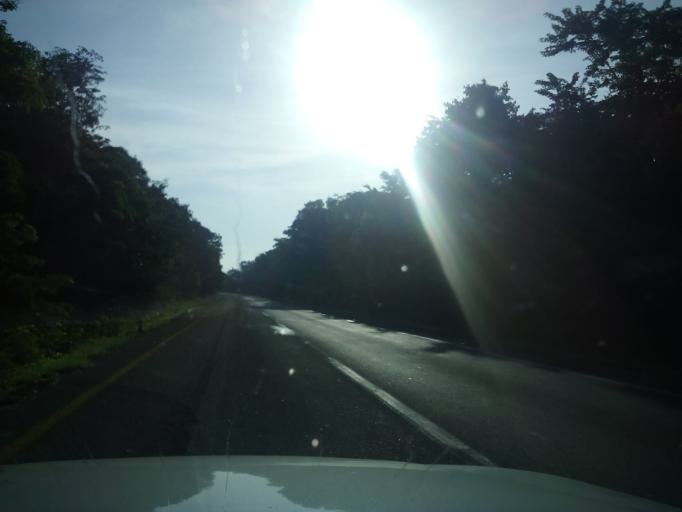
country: MX
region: Yucatan
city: Tinum
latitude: 20.7084
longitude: -88.4615
